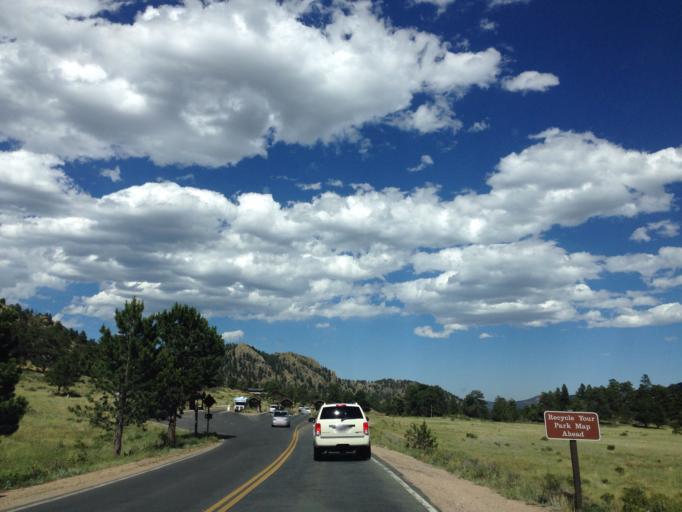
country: US
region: Colorado
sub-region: Larimer County
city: Estes Park
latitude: 40.3658
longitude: -105.5826
